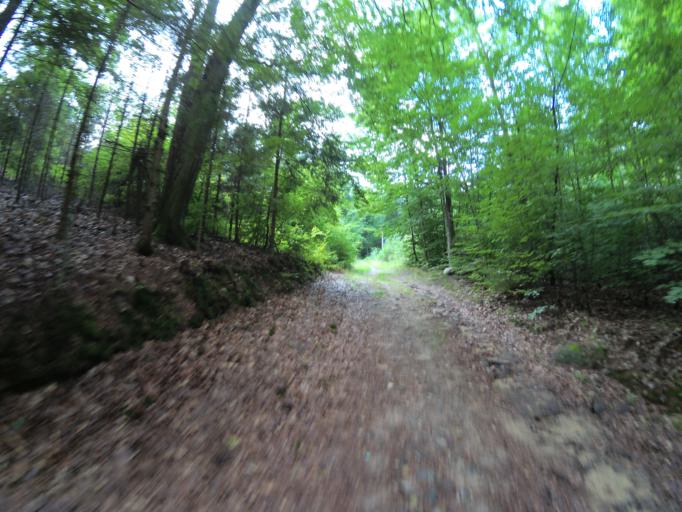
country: PL
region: Pomeranian Voivodeship
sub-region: Gdynia
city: Wielki Kack
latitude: 54.5049
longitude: 18.4386
